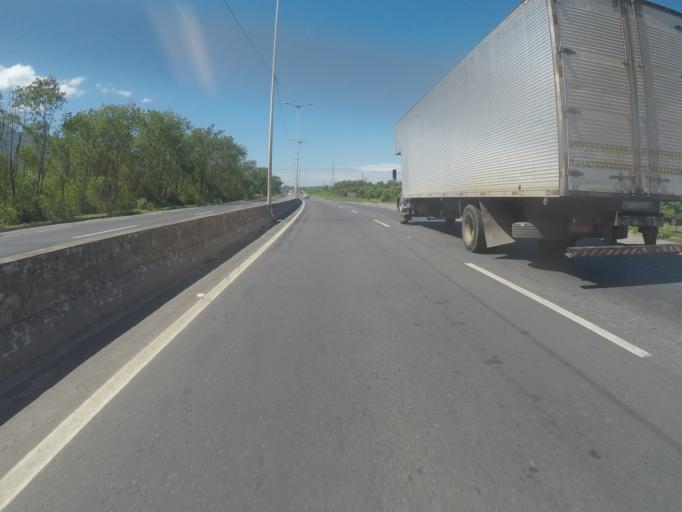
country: BR
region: Espirito Santo
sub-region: Serra
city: Serra
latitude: -20.2158
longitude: -40.3250
